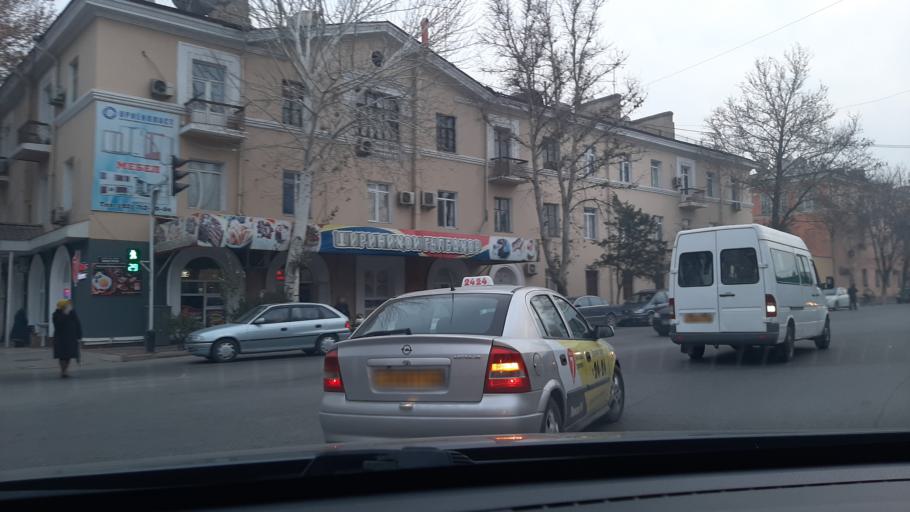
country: TJ
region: Viloyati Sughd
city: Khujand
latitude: 40.2735
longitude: 69.6391
